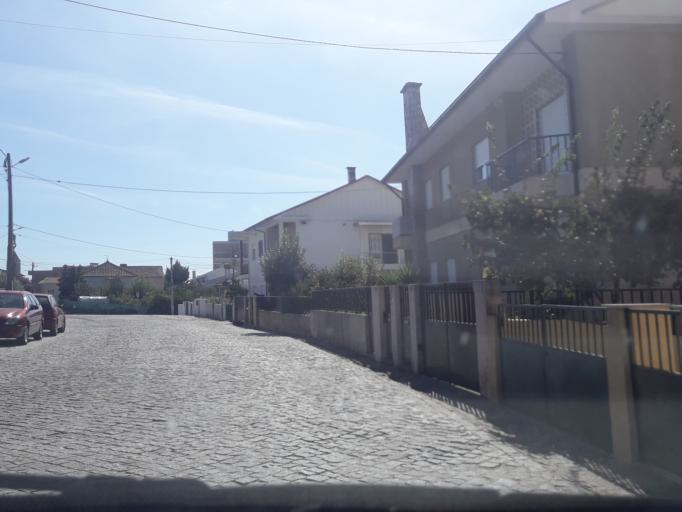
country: PT
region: Braga
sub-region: Braga
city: Braga
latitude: 41.5347
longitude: -8.4076
